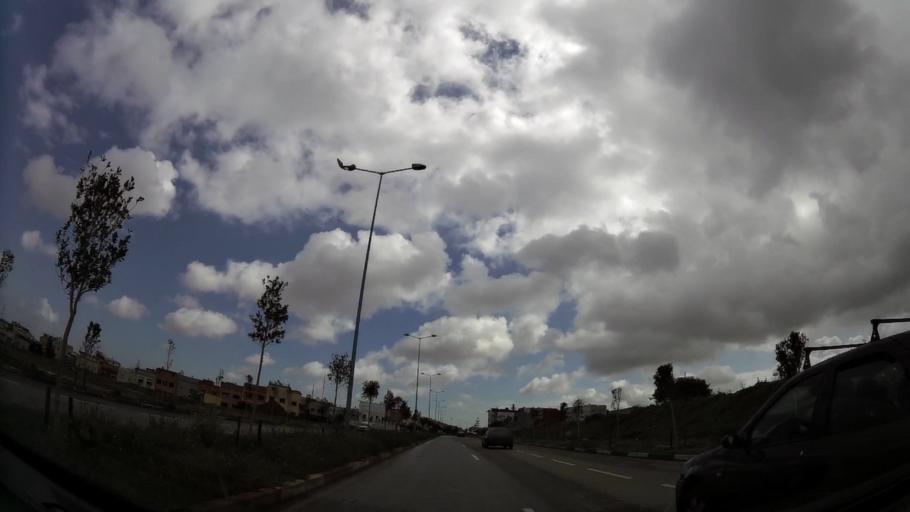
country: MA
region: Grand Casablanca
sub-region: Casablanca
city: Casablanca
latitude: 33.5303
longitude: -7.5911
